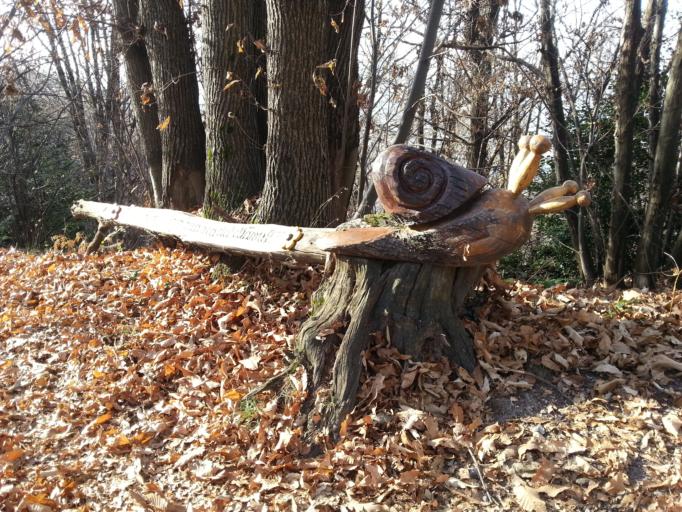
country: IT
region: Lombardy
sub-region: Provincia di Como
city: Maslianico
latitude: 45.8558
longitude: 9.0513
